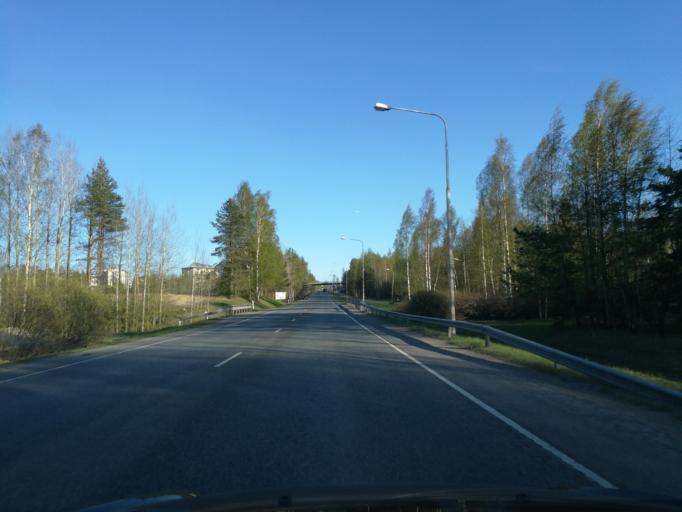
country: FI
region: Uusimaa
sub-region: Helsinki
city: Tuusula
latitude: 60.4004
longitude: 25.0135
